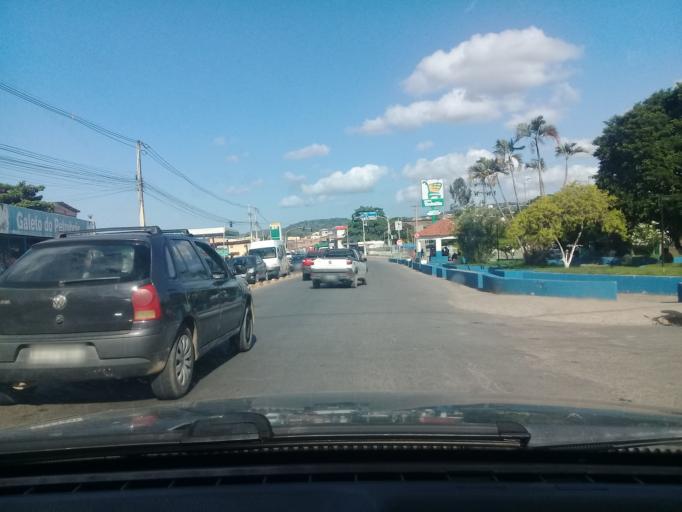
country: BR
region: Pernambuco
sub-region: Vitoria De Santo Antao
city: Vitoria de Santo Antao
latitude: -8.1136
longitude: -35.2860
